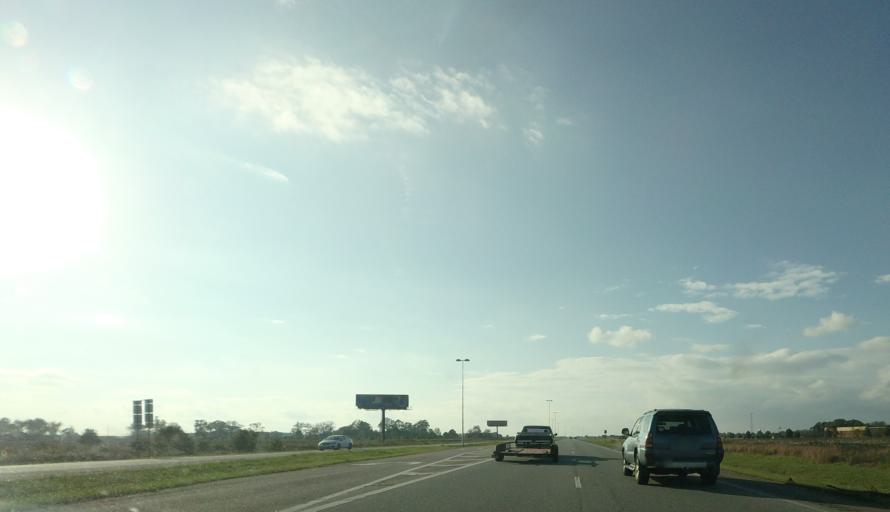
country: US
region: Georgia
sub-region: Houston County
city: Centerville
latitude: 32.5809
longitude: -83.7218
